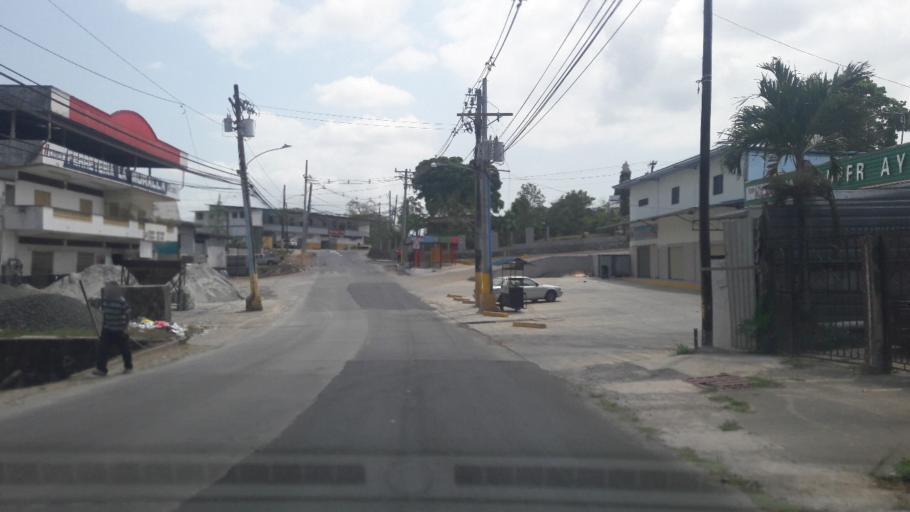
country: PA
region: Panama
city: La Cabima
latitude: 9.1244
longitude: -79.5447
